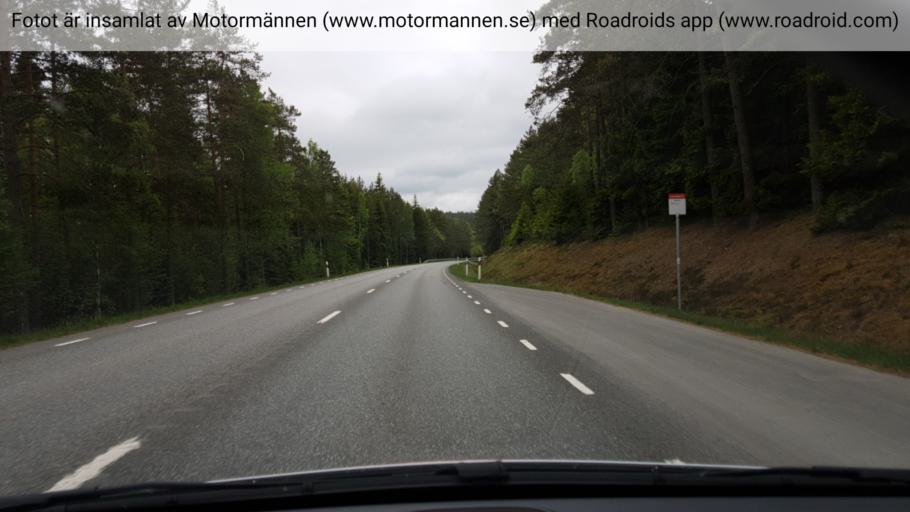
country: SE
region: Joenkoeping
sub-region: Mullsjo Kommun
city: Mullsjoe
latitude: 57.6841
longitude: 13.8483
